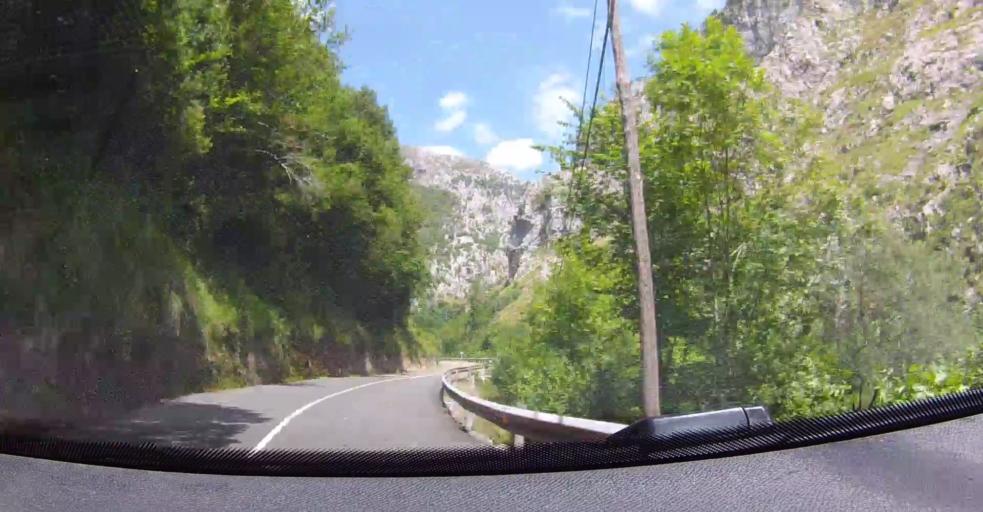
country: ES
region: Cantabria
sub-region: Provincia de Cantabria
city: Tresviso
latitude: 43.2819
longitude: -4.6270
